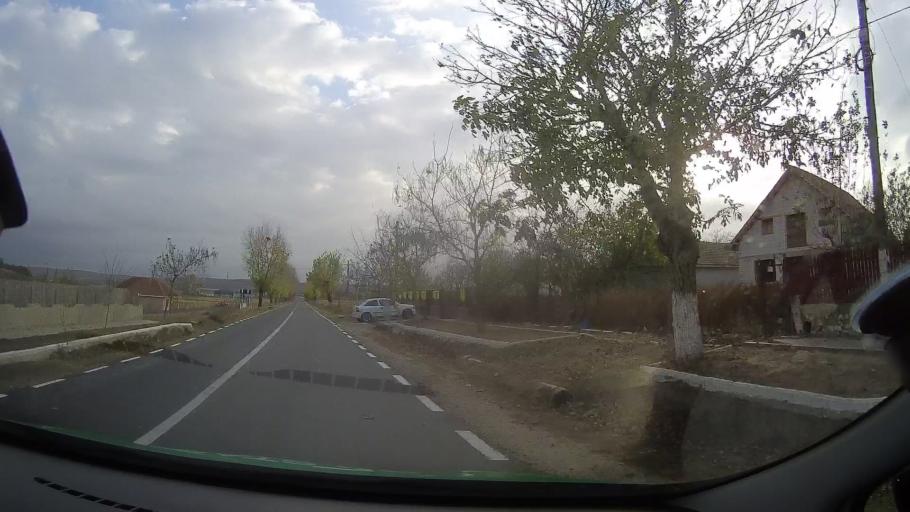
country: RO
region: Constanta
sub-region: Comuna Mircea Voda
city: Mircea Voda
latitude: 44.2752
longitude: 28.1718
